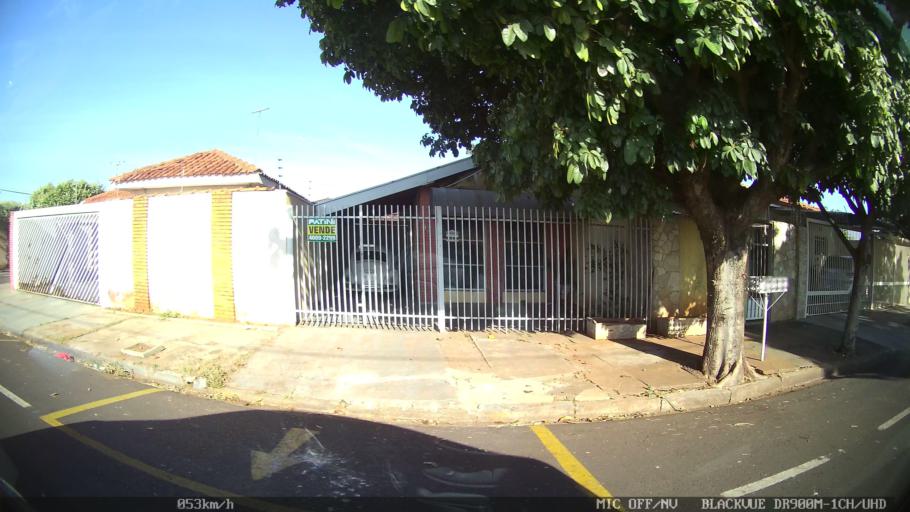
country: BR
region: Sao Paulo
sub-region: Sao Jose Do Rio Preto
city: Sao Jose do Rio Preto
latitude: -20.8179
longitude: -49.4057
